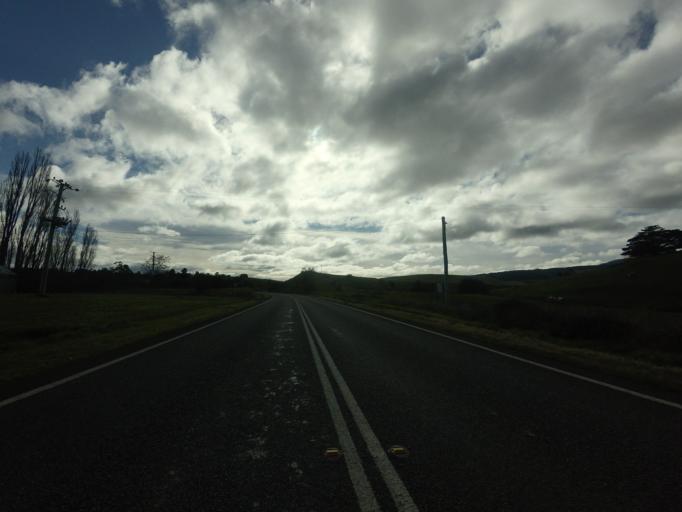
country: AU
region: Tasmania
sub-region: Derwent Valley
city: New Norfolk
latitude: -42.6888
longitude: 146.9418
